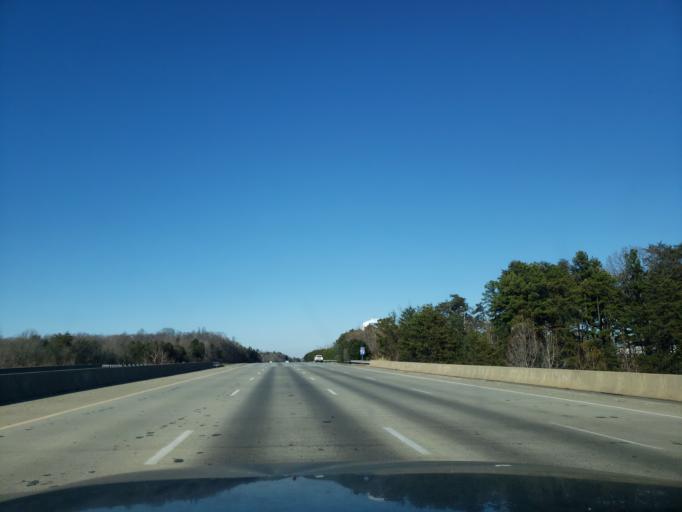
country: US
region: North Carolina
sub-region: Guilford County
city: High Point
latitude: 35.9663
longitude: -79.9746
